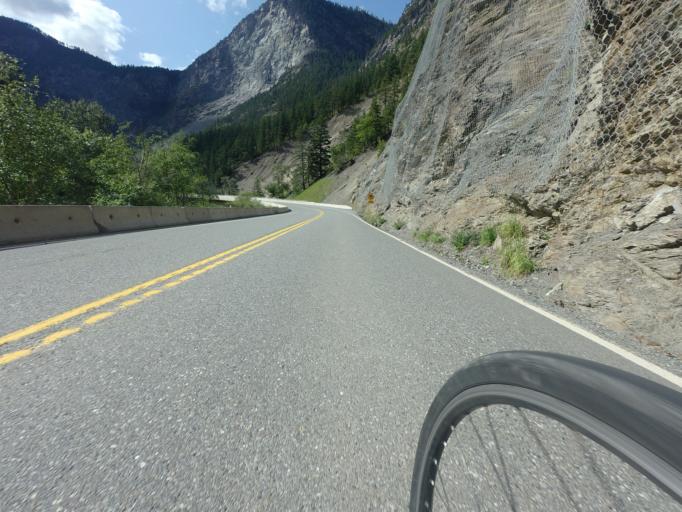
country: CA
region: British Columbia
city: Lillooet
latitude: 50.6434
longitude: -122.0526
